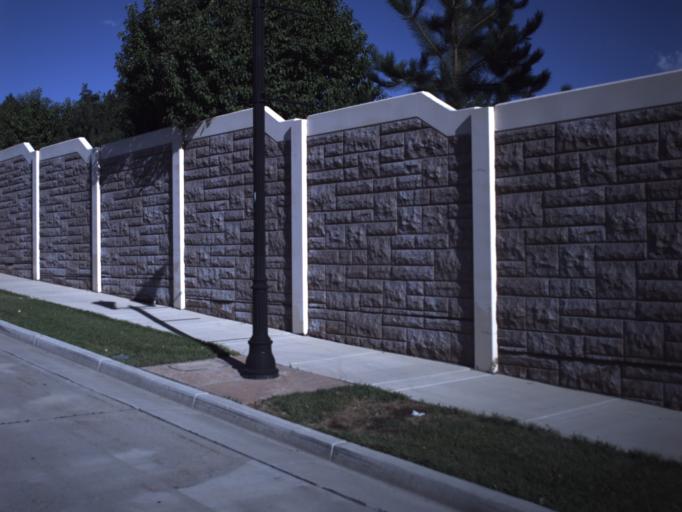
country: US
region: Utah
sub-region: Salt Lake County
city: South Jordan
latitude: 40.5443
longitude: -111.9227
